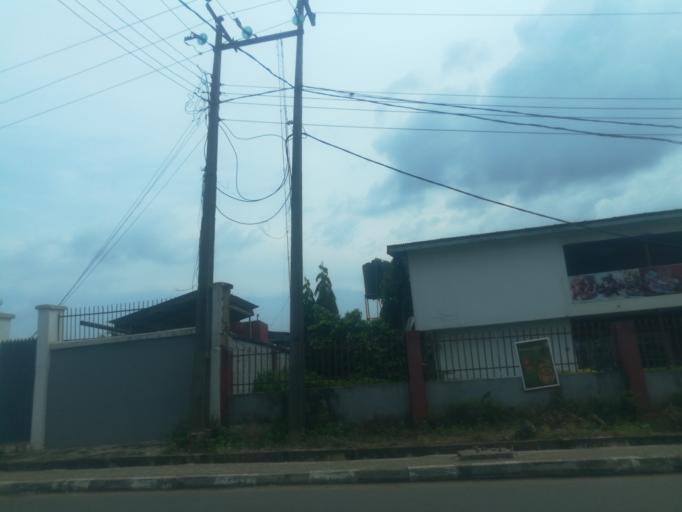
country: NG
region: Oyo
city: Ibadan
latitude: 7.3651
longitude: 3.8577
